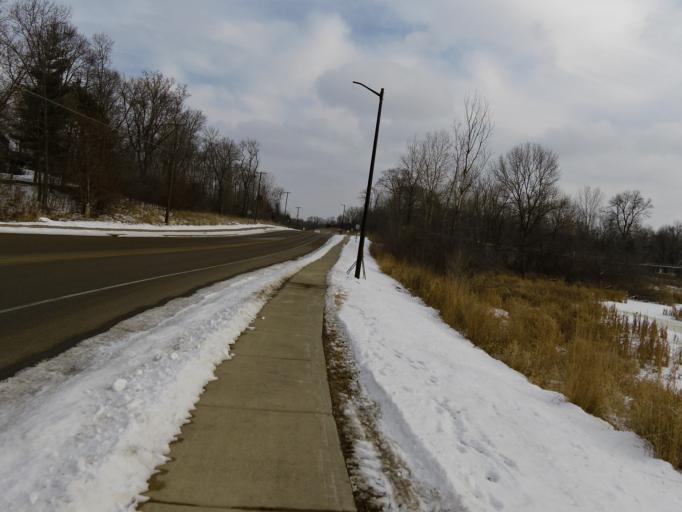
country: US
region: Minnesota
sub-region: Scott County
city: Prior Lake
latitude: 44.7074
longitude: -93.4768
